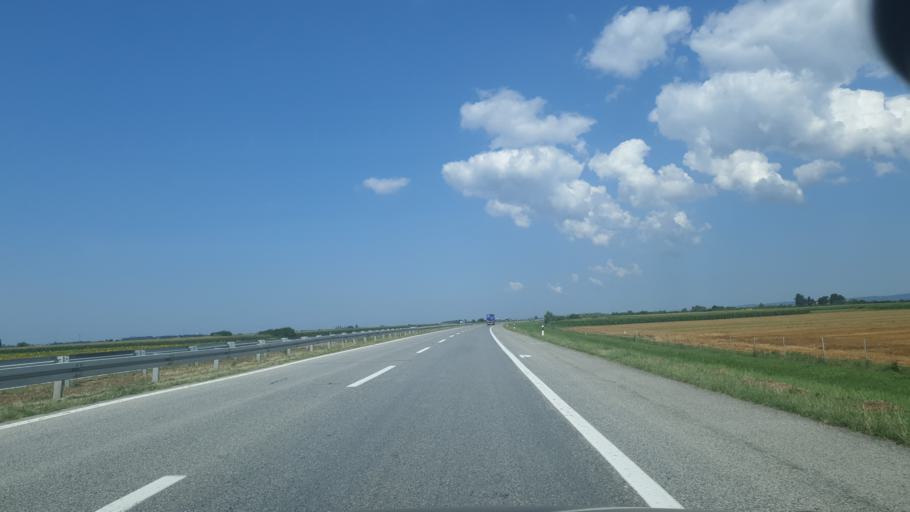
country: RS
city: Sasinci
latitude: 44.9802
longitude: 19.7292
